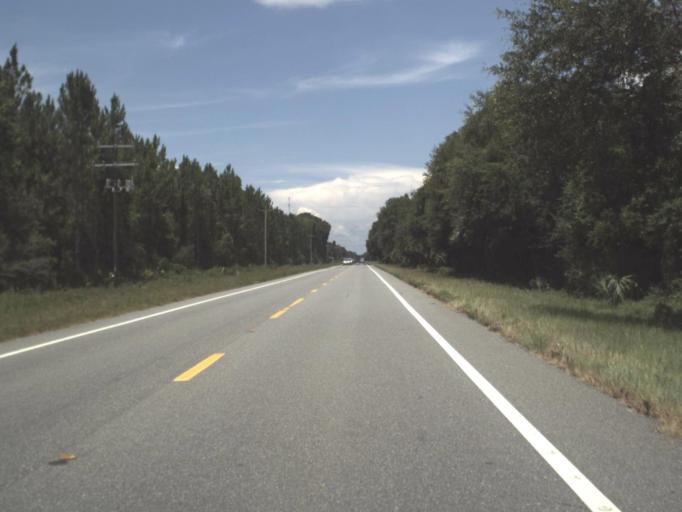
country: US
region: Florida
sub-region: Taylor County
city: Perry
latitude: 30.1411
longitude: -83.8940
